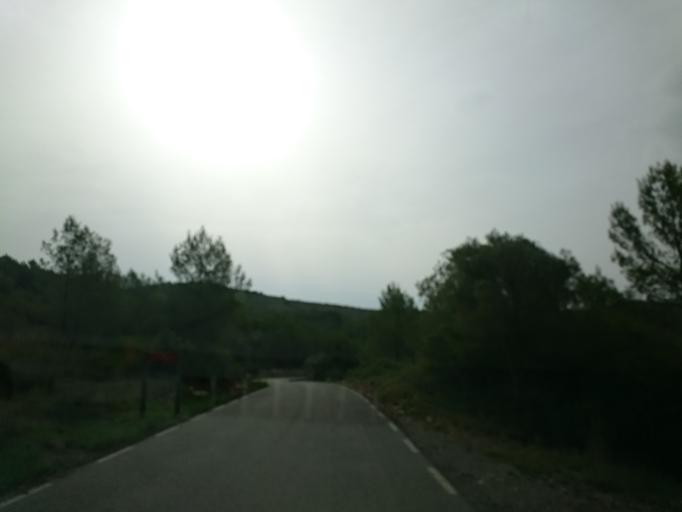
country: ES
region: Catalonia
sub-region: Provincia de Barcelona
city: Olivella
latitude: 41.3067
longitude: 1.8196
